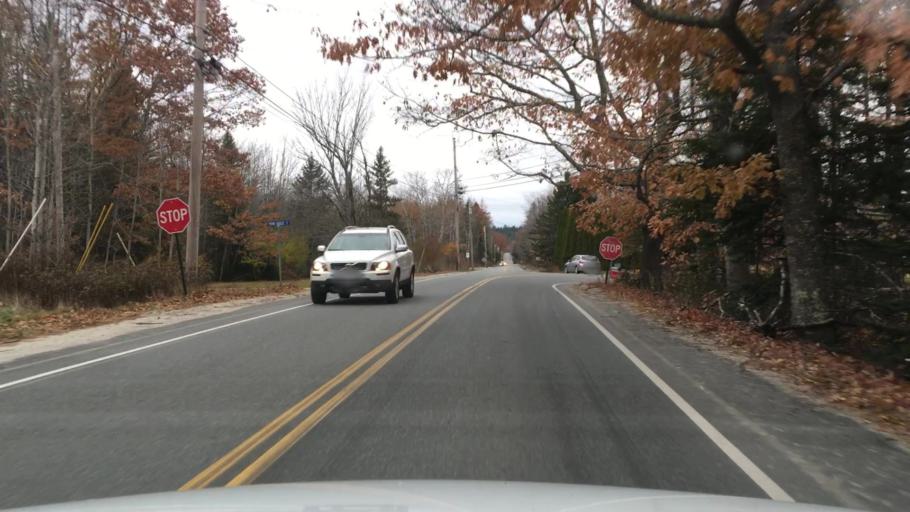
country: US
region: Maine
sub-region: Hancock County
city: Sedgwick
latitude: 44.4142
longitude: -68.6074
